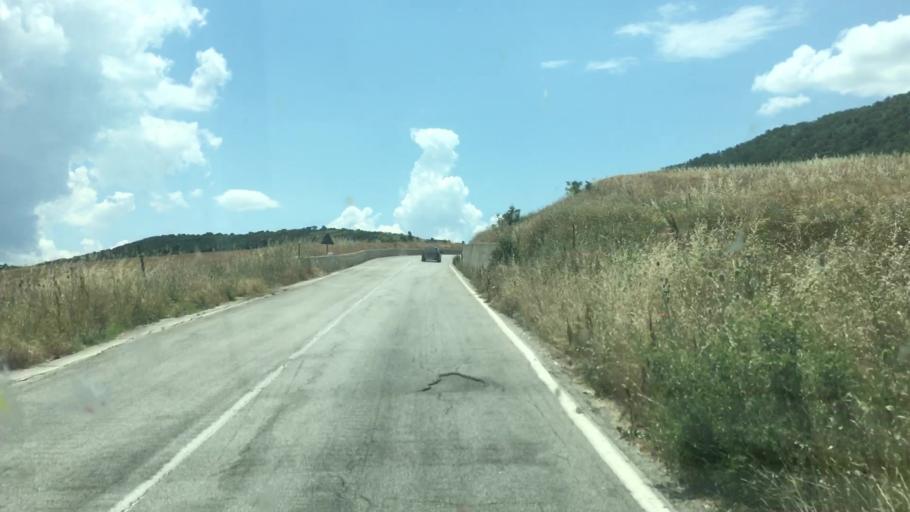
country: IT
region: Basilicate
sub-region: Provincia di Potenza
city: Tolve
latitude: 40.6887
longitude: 15.9842
